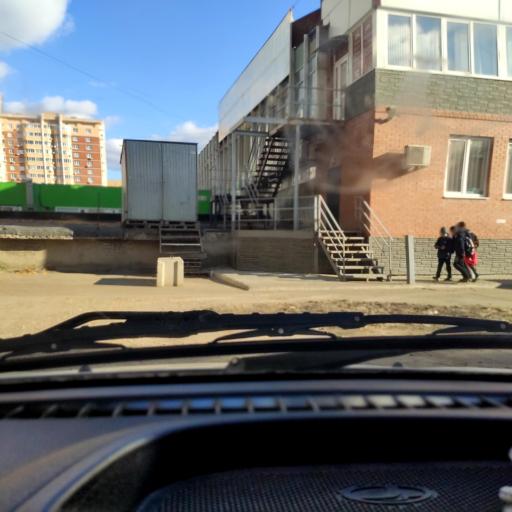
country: RU
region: Samara
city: Tol'yatti
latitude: 53.5270
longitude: 49.2737
